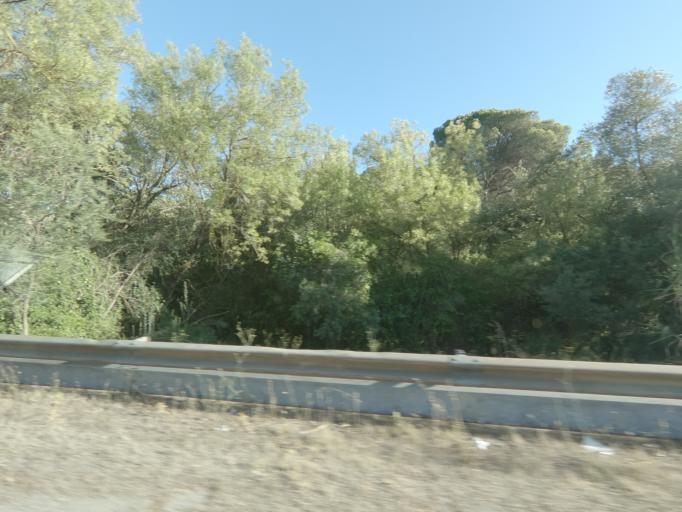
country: PT
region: Setubal
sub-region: Setubal
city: Setubal
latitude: 38.5037
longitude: -8.9466
